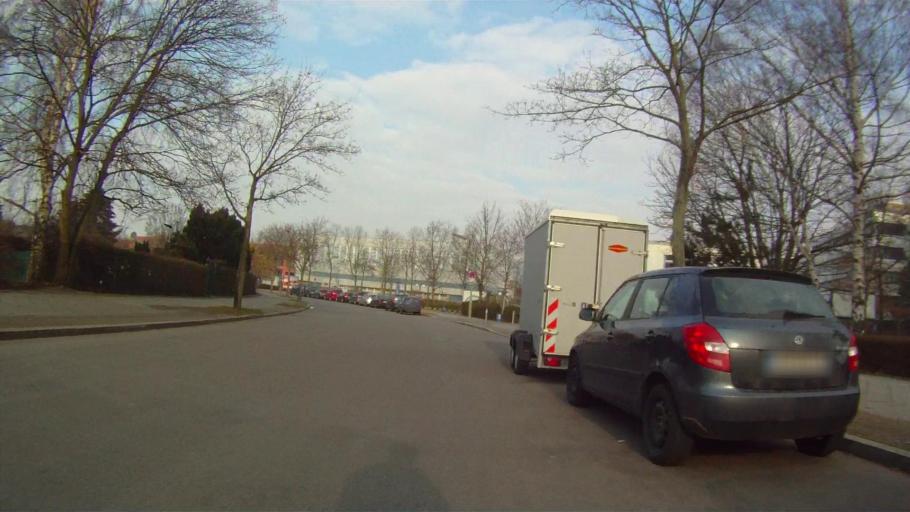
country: DE
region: Berlin
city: Britz
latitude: 52.4570
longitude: 13.4524
